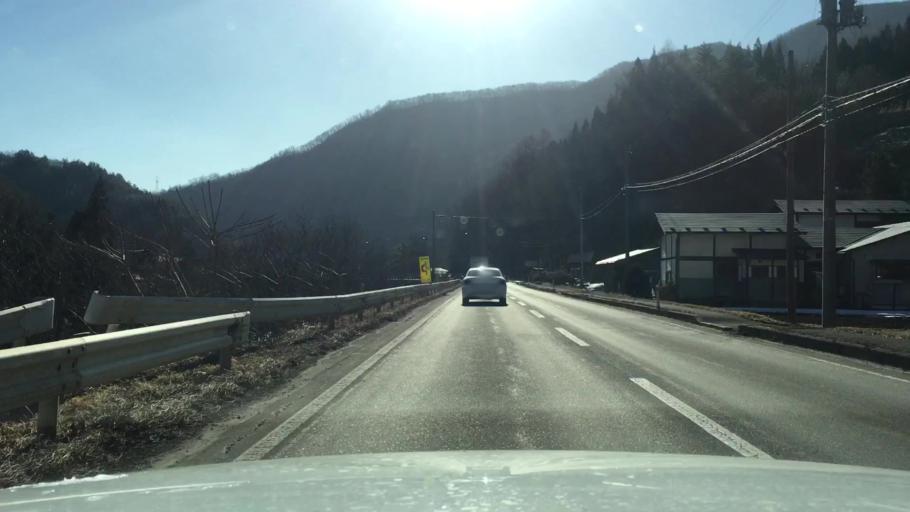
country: JP
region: Iwate
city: Tono
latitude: 39.6171
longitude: 141.6243
